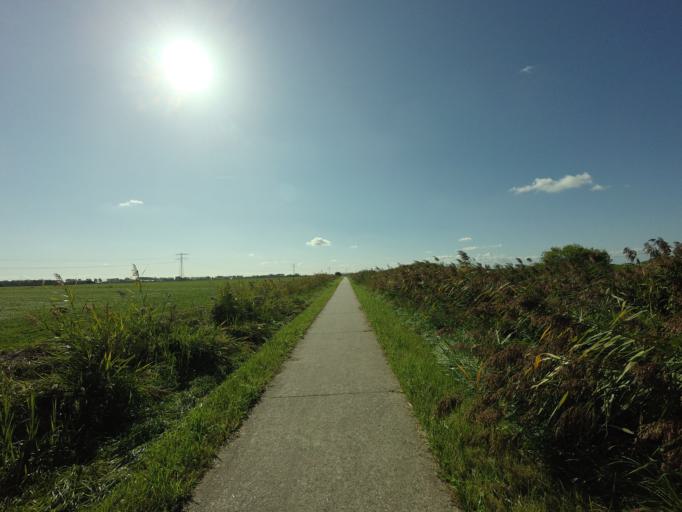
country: NL
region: Friesland
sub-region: Gemeente Boarnsterhim
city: Reduzum
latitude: 53.1466
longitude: 5.7639
